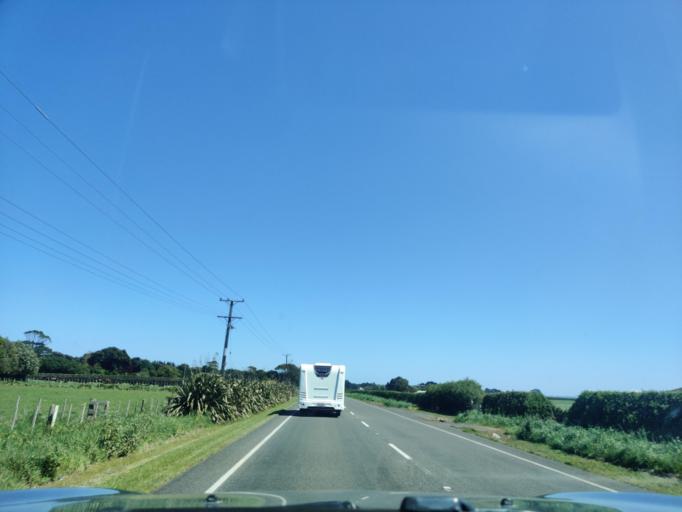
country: NZ
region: Manawatu-Wanganui
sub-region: Wanganui District
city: Wanganui
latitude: -39.8116
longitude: 174.7851
